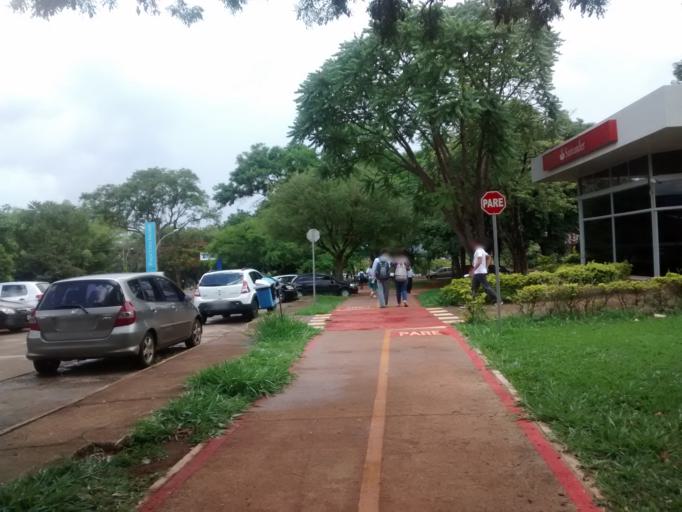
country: BR
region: Federal District
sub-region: Brasilia
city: Brasilia
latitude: -15.7667
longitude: -47.8707
